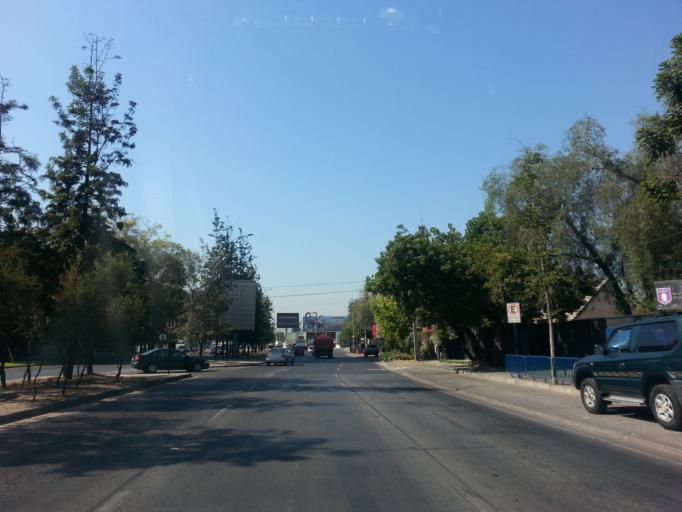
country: CL
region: Santiago Metropolitan
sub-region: Provincia de Santiago
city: Villa Presidente Frei, Nunoa, Santiago, Chile
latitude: -33.4361
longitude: -70.5741
